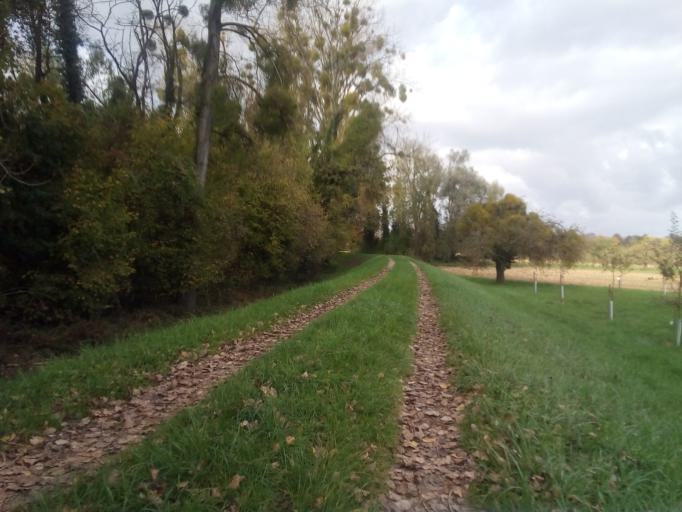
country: DE
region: Baden-Wuerttemberg
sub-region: Karlsruhe Region
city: Lichtenau
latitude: 48.7180
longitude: 7.9763
